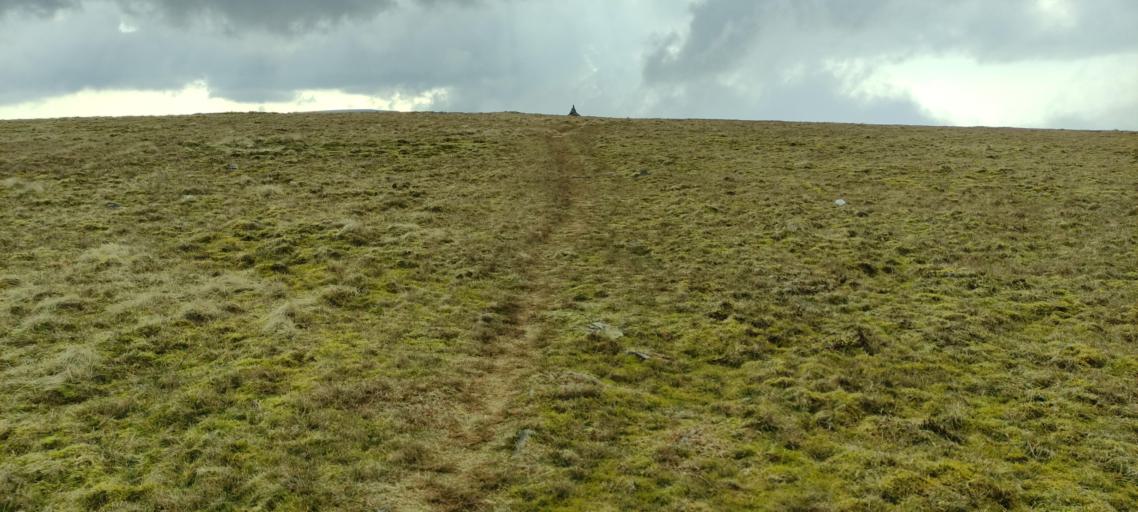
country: GB
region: England
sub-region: Cumbria
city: Appleby-in-Westmorland
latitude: 54.7367
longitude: -2.5426
